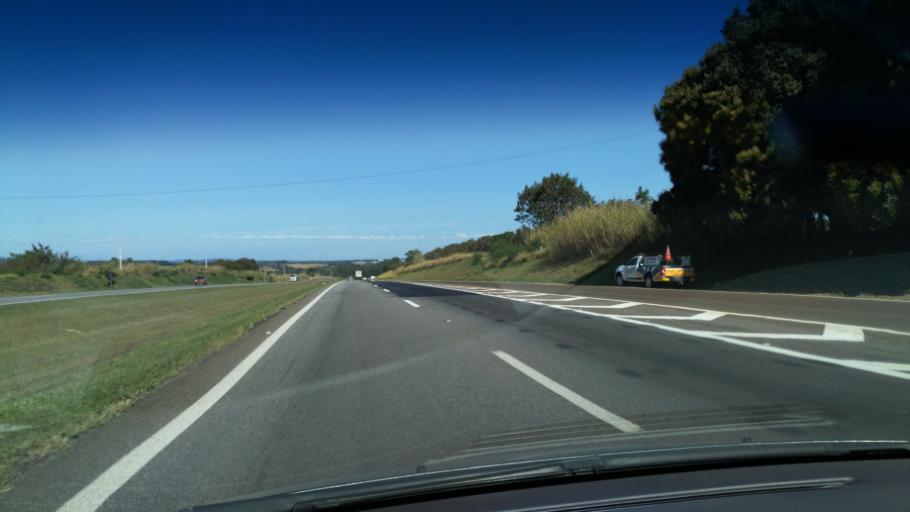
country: BR
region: Sao Paulo
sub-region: Santo Antonio De Posse
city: Santo Antonio de Posse
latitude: -22.5484
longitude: -46.9990
